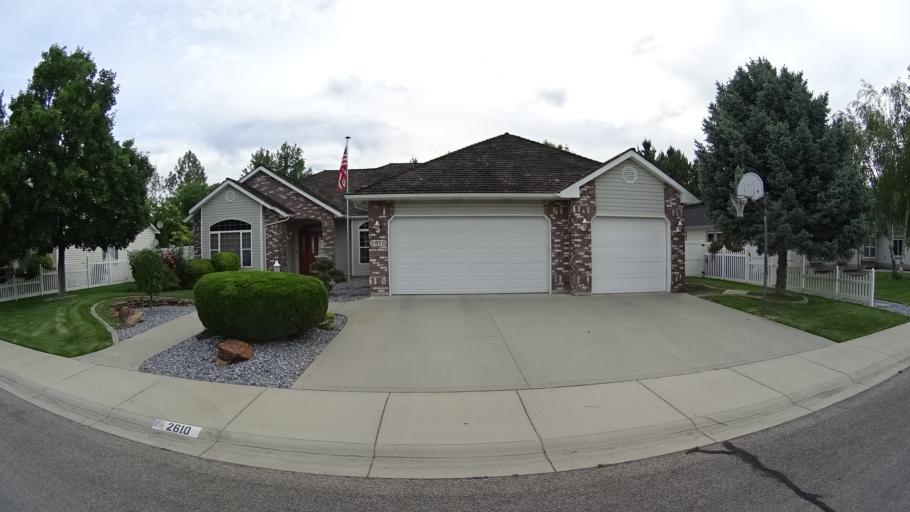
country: US
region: Idaho
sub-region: Ada County
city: Meridian
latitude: 43.5800
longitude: -116.3884
